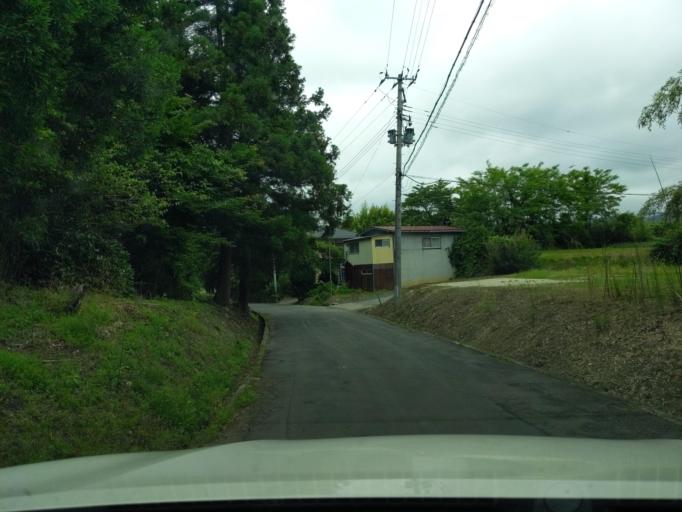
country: JP
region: Fukushima
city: Koriyama
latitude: 37.4653
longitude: 140.3078
